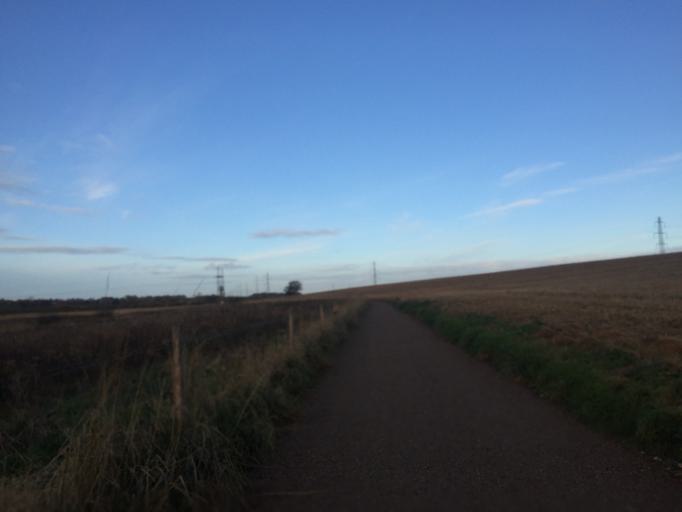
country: DK
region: Zealand
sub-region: Ringsted Kommune
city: Ringsted
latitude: 55.4519
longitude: 11.7677
